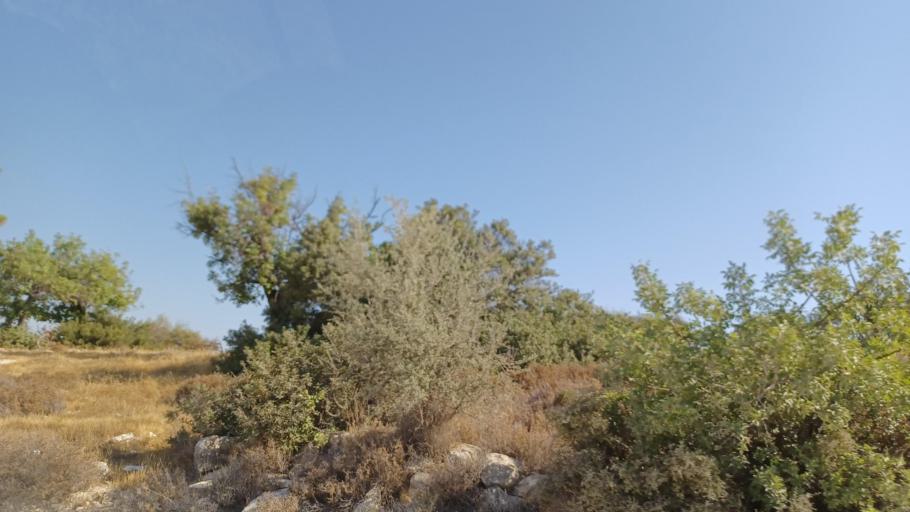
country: CY
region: Limassol
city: Pissouri
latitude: 34.7283
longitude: 32.6760
